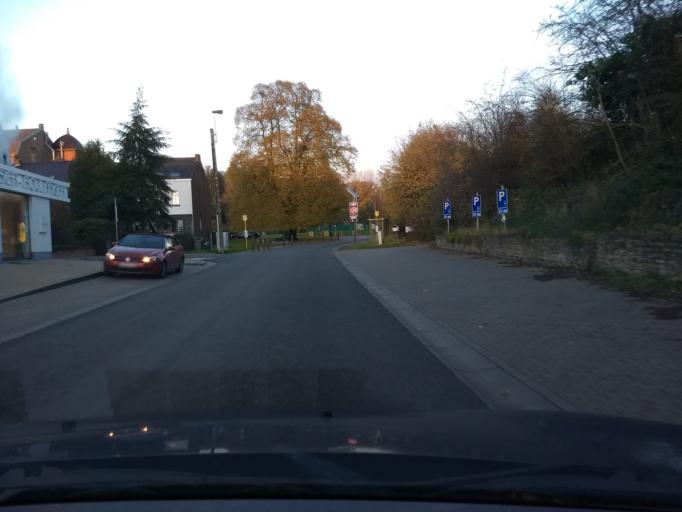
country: BE
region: Wallonia
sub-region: Province du Brabant Wallon
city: Ittre
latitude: 50.6488
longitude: 4.2648
